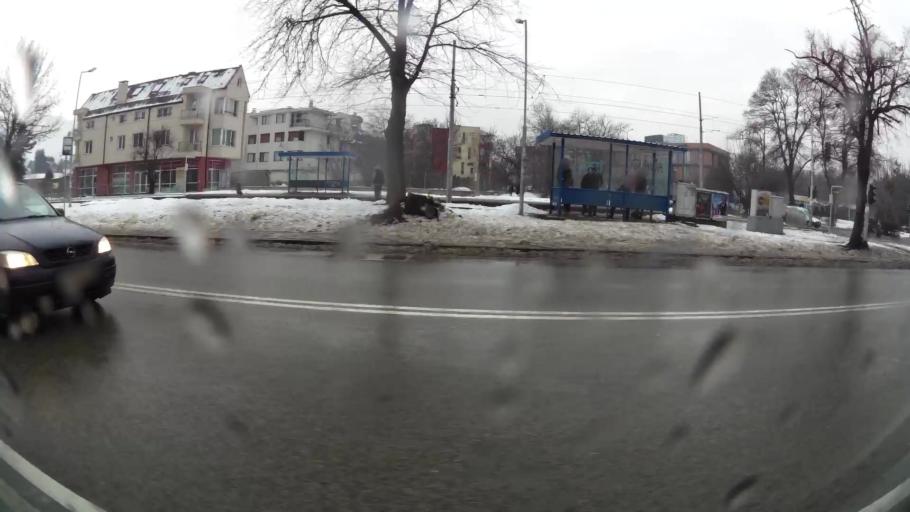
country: BG
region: Sofia-Capital
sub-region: Stolichna Obshtina
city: Sofia
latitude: 42.6769
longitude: 23.2682
